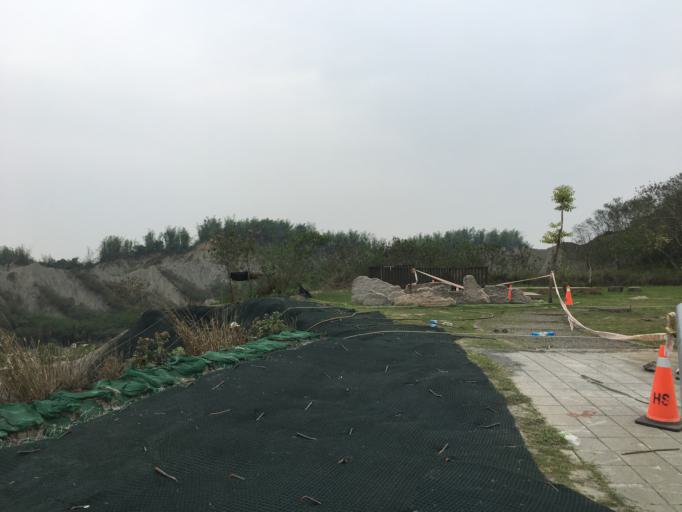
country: TW
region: Taiwan
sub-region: Tainan
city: Tainan
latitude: 22.8873
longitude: 120.3887
